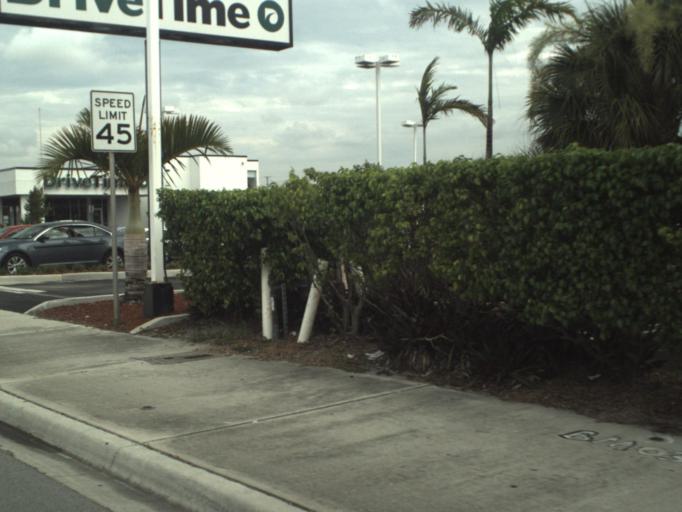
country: US
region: Florida
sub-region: Palm Beach County
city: Schall Circle
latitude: 26.7067
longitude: -80.0946
